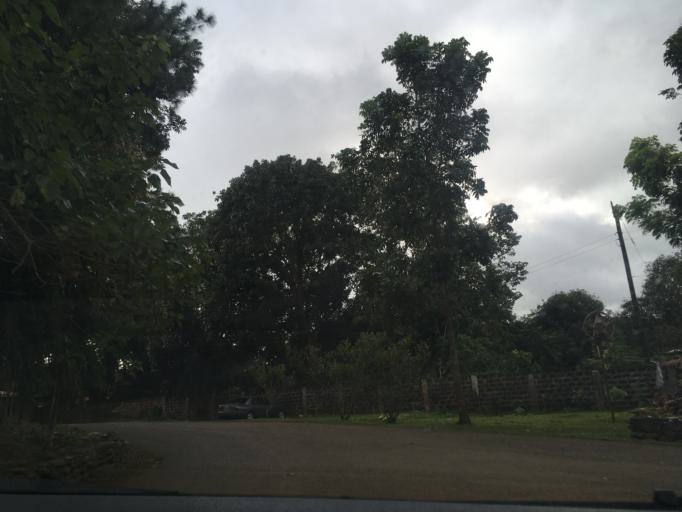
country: PH
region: Calabarzon
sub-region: Province of Rizal
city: Sampaloc
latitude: 14.5347
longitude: 121.3629
